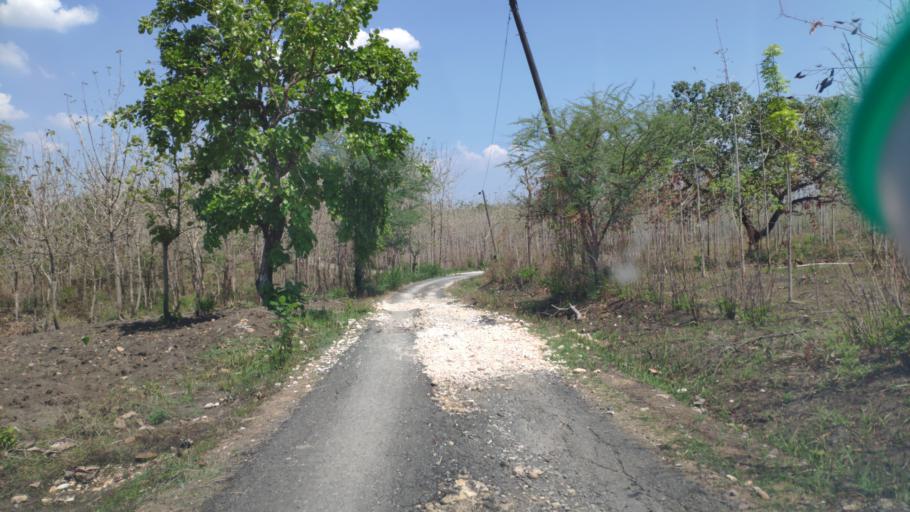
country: ID
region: Central Java
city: Galuk
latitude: -7.1075
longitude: 111.4952
